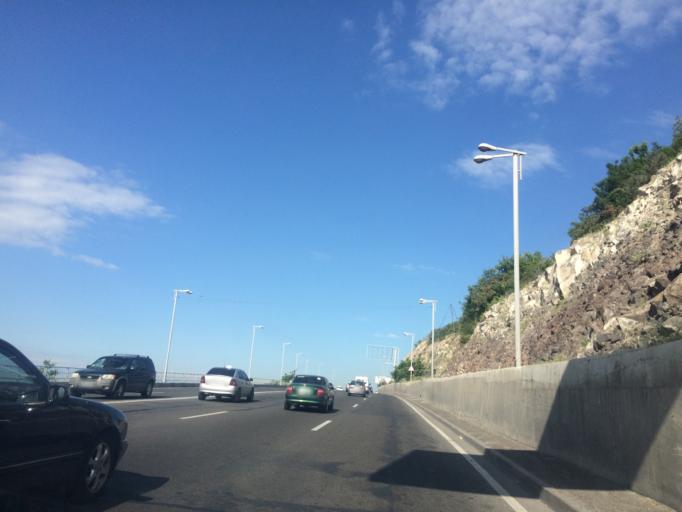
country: AM
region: Yerevan
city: Yerevan
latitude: 40.1942
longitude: 44.5249
